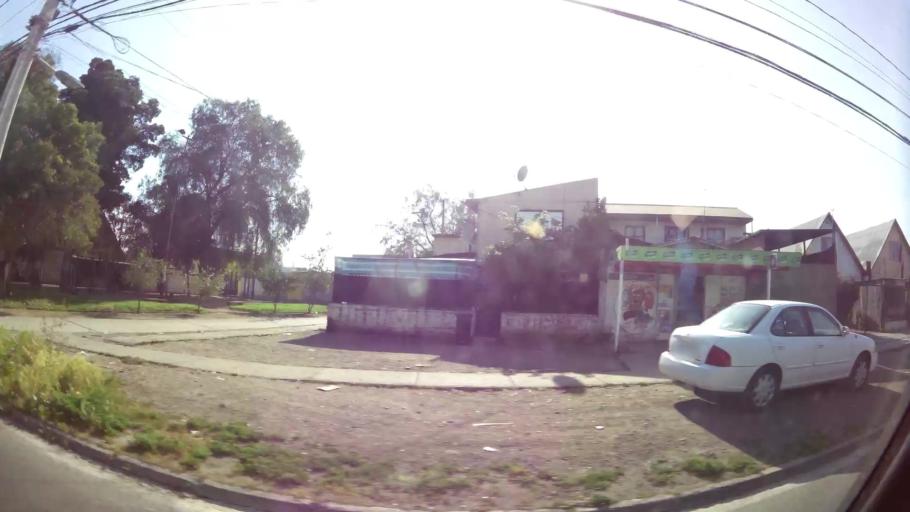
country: CL
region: Santiago Metropolitan
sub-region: Provincia de Santiago
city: Lo Prado
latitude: -33.4188
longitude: -70.7565
